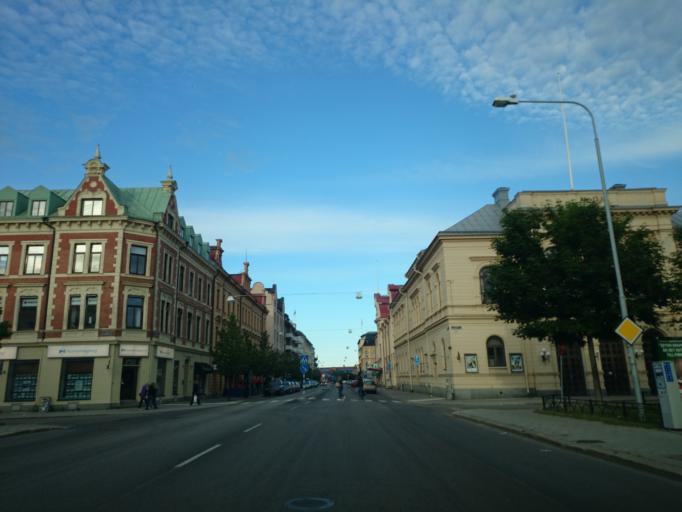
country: SE
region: Vaesternorrland
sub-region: Sundsvalls Kommun
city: Sundsvall
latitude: 62.3888
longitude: 17.3073
